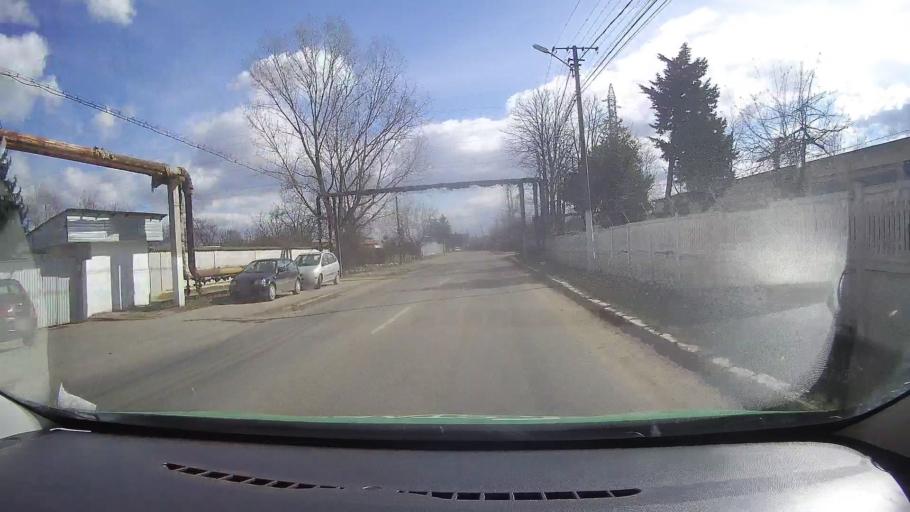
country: RO
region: Dambovita
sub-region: Municipiul Targoviste
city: Targoviste
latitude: 44.9418
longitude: 25.4397
